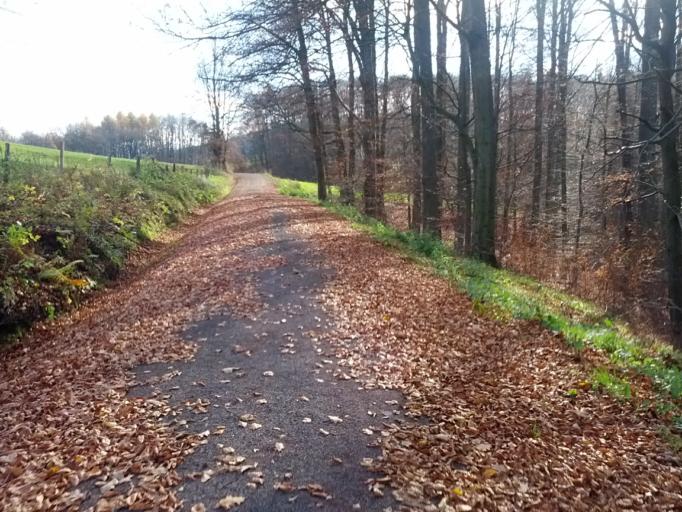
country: DE
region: Thuringia
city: Krauthausen
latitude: 50.9982
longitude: 10.2282
